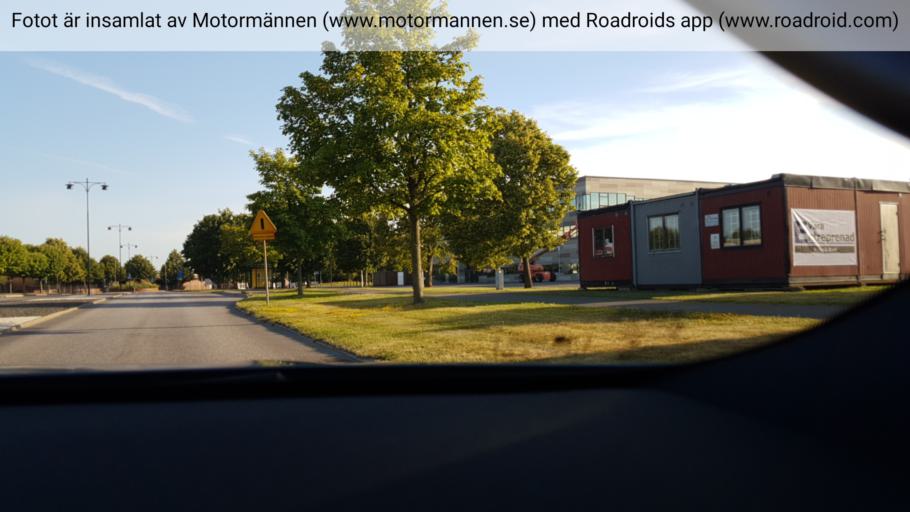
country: SE
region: Vaestra Goetaland
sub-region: Skara Kommun
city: Skara
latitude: 58.3871
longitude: 13.4513
